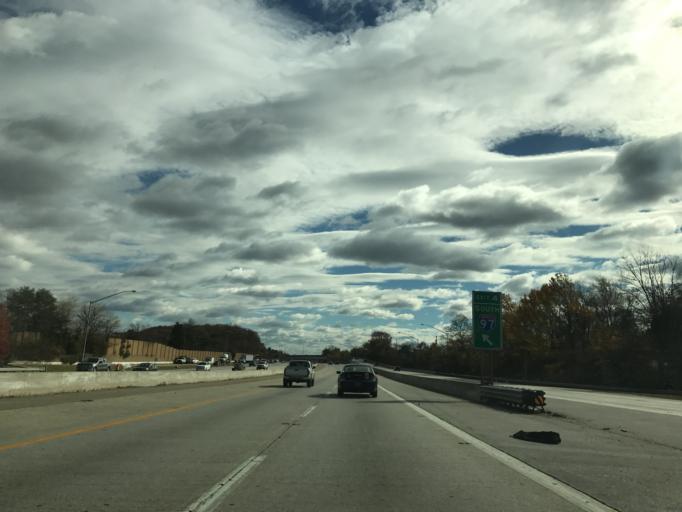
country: US
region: Maryland
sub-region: Anne Arundel County
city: Linthicum
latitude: 39.2053
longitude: -76.6404
